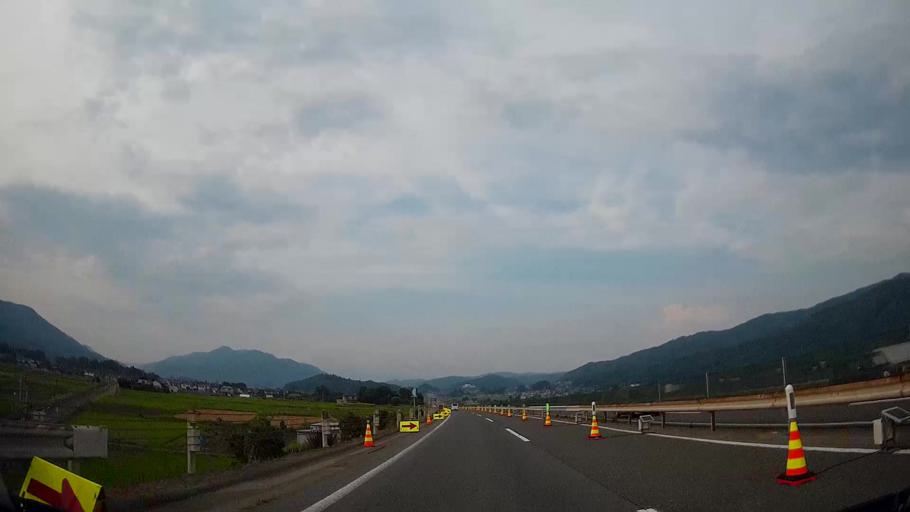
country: JP
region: Nagano
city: Tatsuno
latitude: 35.9488
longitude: 137.9868
